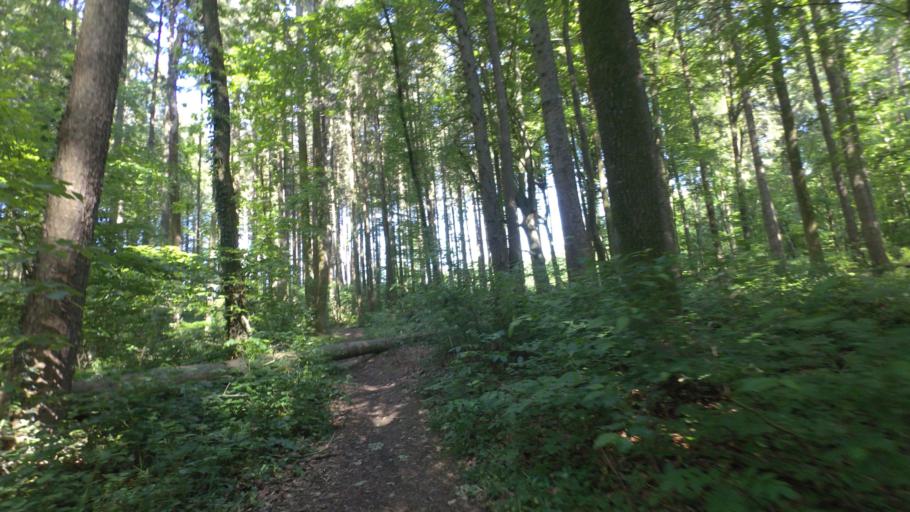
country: DE
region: Bavaria
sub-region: Upper Bavaria
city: Seeon-Seebruck
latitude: 47.9250
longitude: 12.4986
